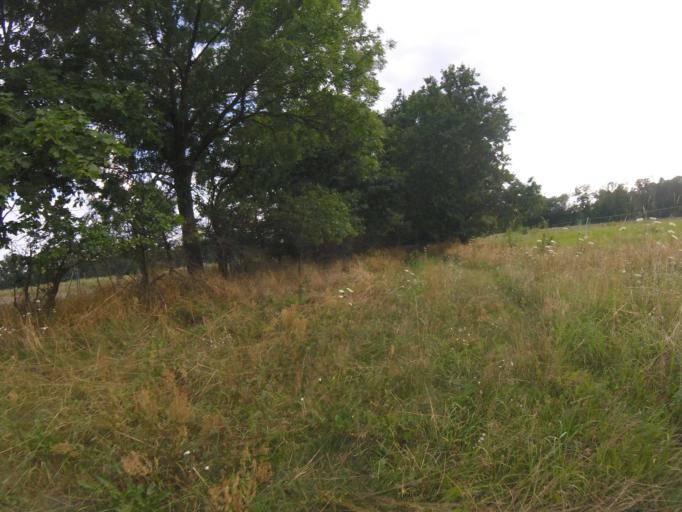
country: DE
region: Brandenburg
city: Mittenwalde
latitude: 52.2920
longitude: 13.5525
